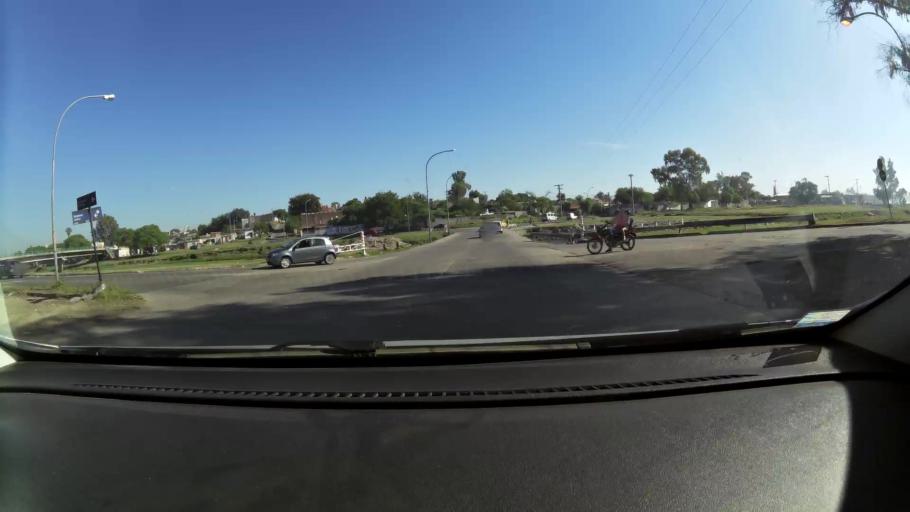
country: AR
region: Cordoba
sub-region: Departamento de Capital
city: Cordoba
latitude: -31.4189
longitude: -64.1501
